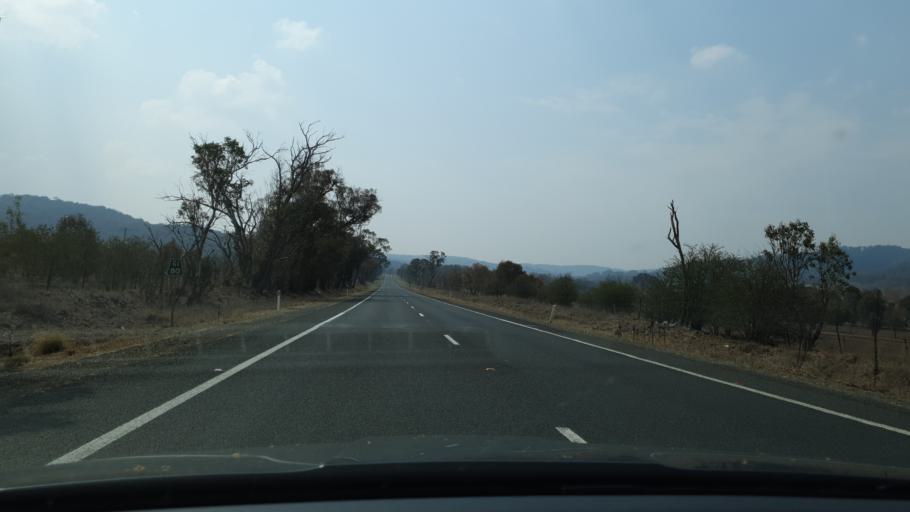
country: AU
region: New South Wales
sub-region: Armidale Dumaresq
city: Armidale
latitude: -30.3750
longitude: 151.6735
